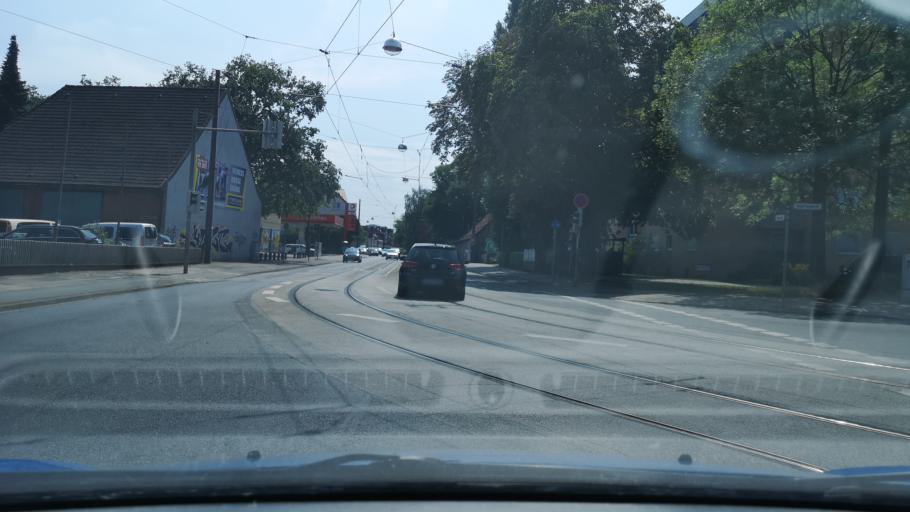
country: DE
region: Lower Saxony
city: Langenhagen
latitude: 52.4152
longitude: 9.7967
